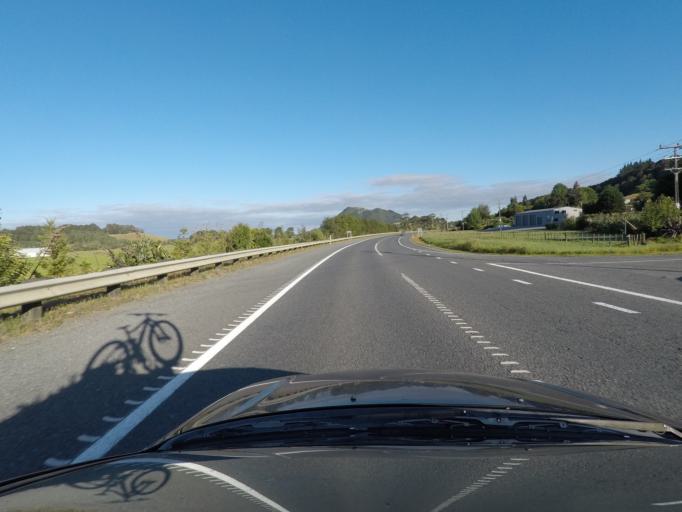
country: NZ
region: Northland
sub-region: Whangarei
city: Whangarei
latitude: -35.6239
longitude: 174.2917
